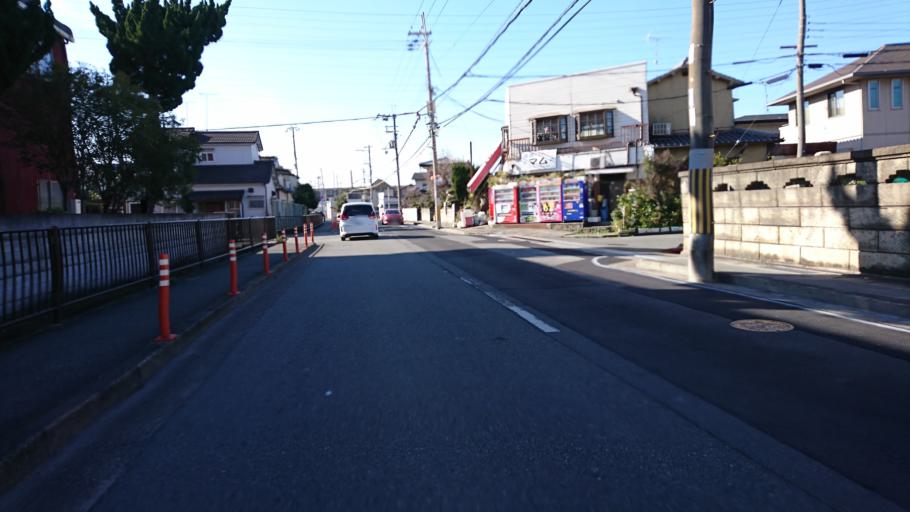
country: JP
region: Hyogo
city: Kakogawacho-honmachi
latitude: 34.7346
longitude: 134.8483
